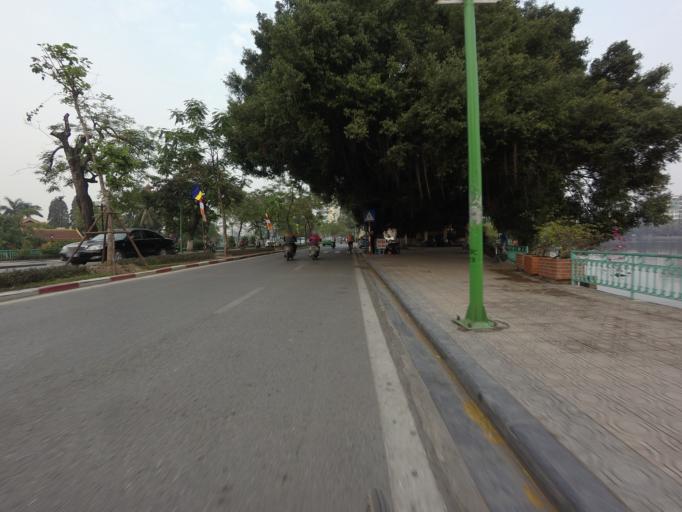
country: VN
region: Ha Noi
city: Hanoi
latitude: 21.0471
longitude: 105.8370
